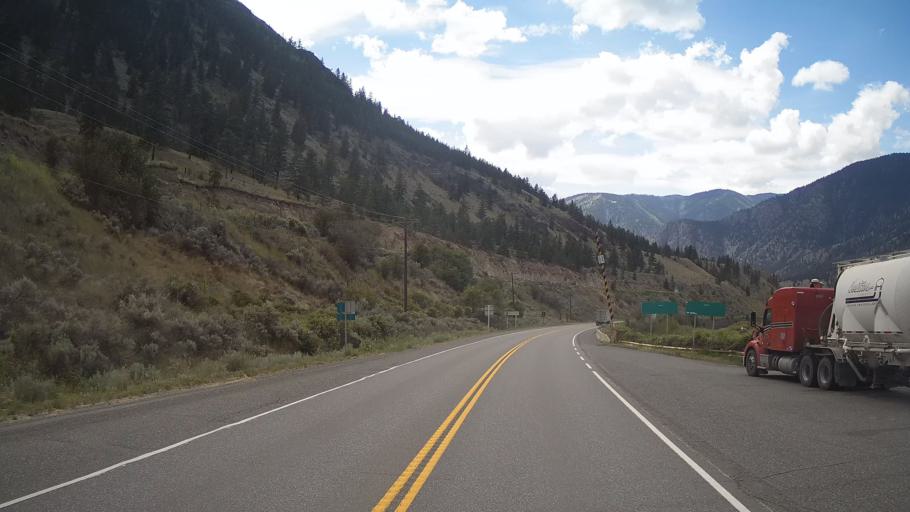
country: CA
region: British Columbia
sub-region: Thompson-Nicola Regional District
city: Ashcroft
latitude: 50.4128
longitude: -121.3604
